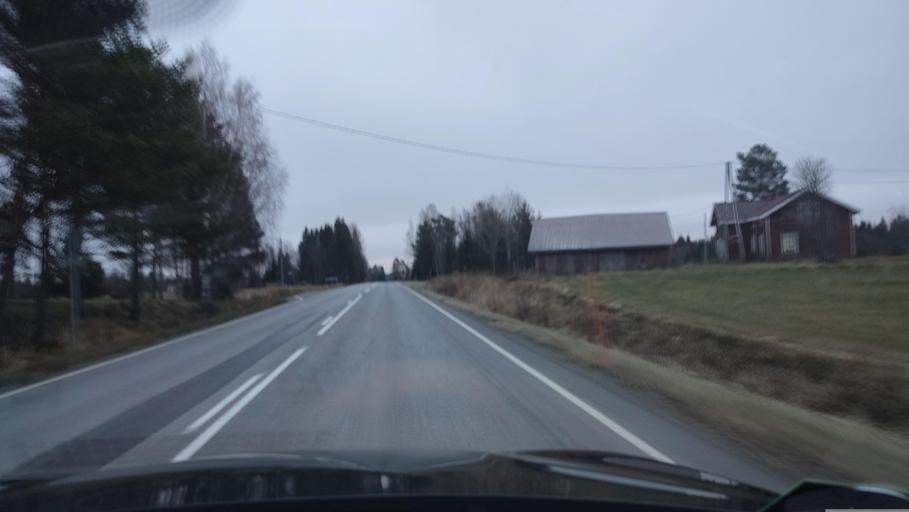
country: FI
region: Southern Ostrobothnia
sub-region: Suupohja
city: Kauhajoki
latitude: 62.3433
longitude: 21.9796
